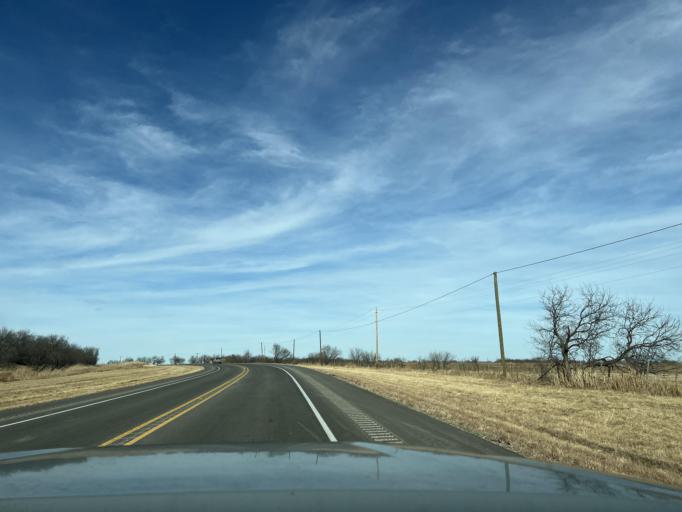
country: US
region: Texas
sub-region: Shackelford County
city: Albany
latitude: 32.5846
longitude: -99.1840
